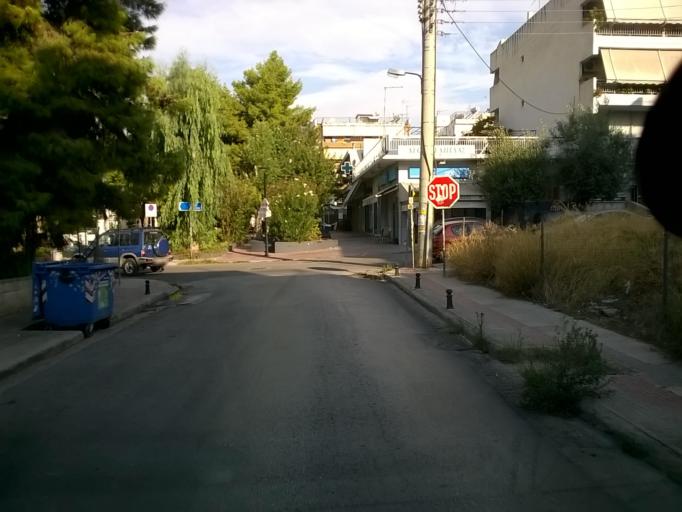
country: GR
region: Attica
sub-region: Nomarchia Athinas
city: Agios Dimitrios
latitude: 37.9294
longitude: 23.7363
